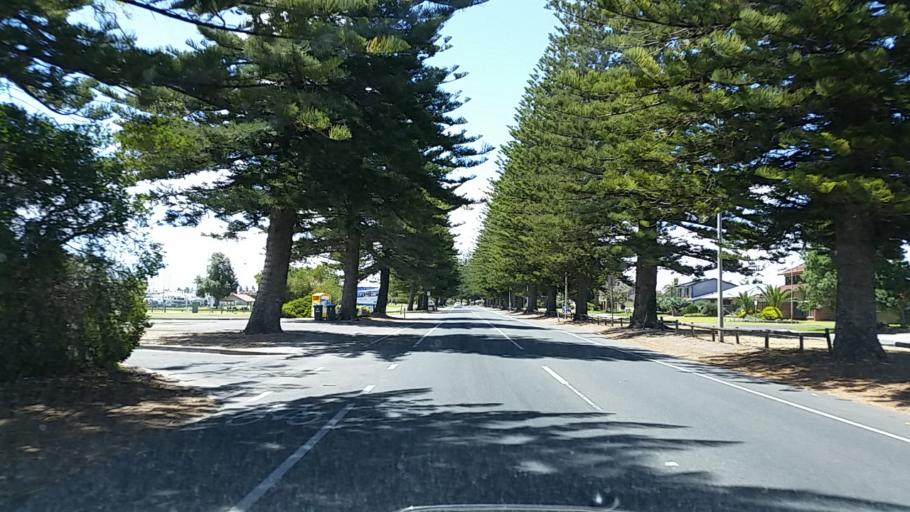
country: AU
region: South Australia
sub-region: Port Adelaide Enfield
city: Birkenhead
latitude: -34.7955
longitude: 138.4916
